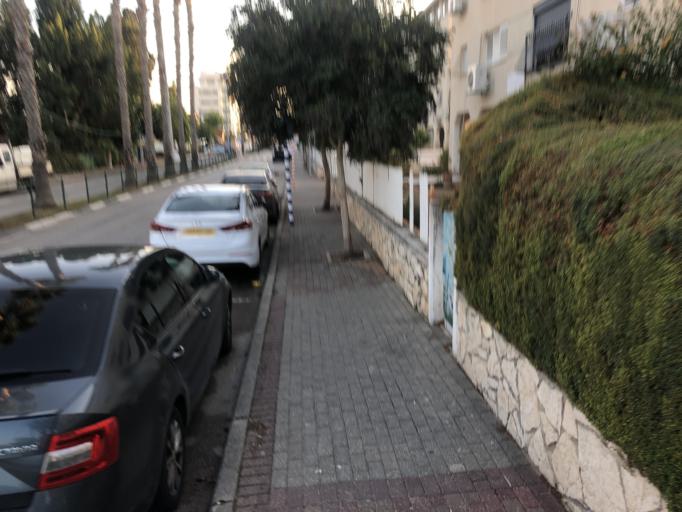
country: IL
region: Northern District
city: `Akko
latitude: 32.9275
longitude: 35.0922
